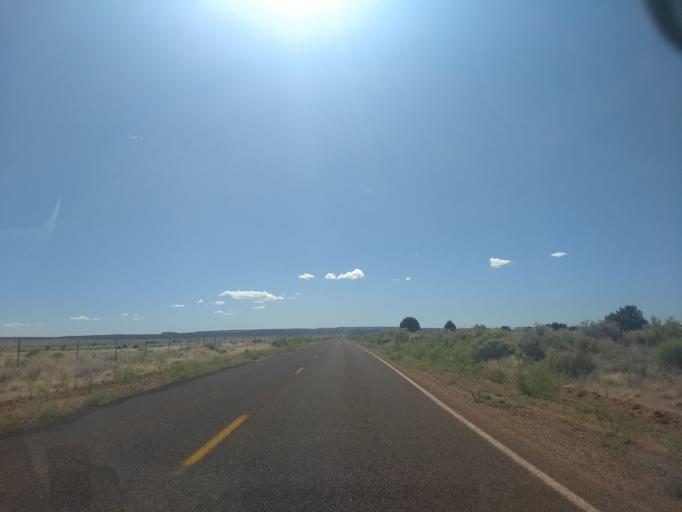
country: US
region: Arizona
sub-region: Mohave County
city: Colorado City
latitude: 36.9468
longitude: -112.9444
